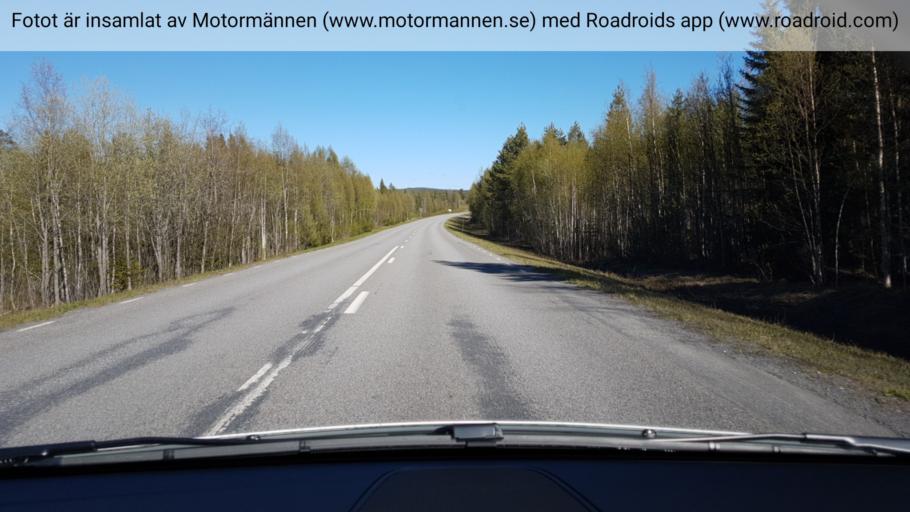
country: SE
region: Jaemtland
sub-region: Stroemsunds Kommun
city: Stroemsund
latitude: 64.3075
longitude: 15.2500
